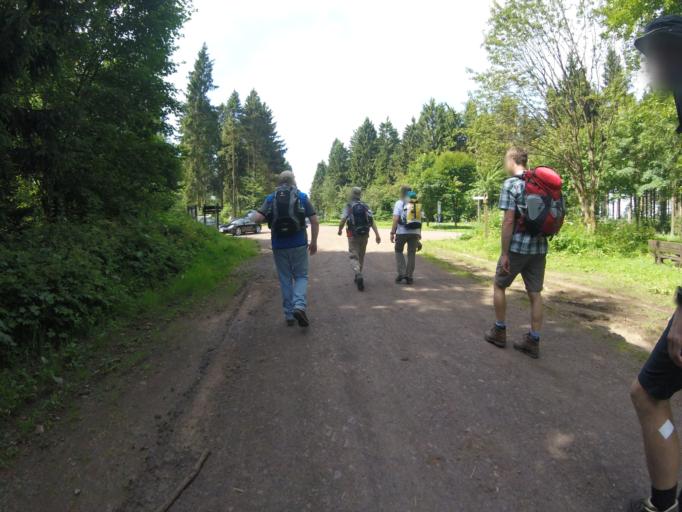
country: DE
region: Hesse
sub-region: Regierungsbezirk Giessen
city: Ulrichstein
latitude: 50.5233
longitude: 9.2373
